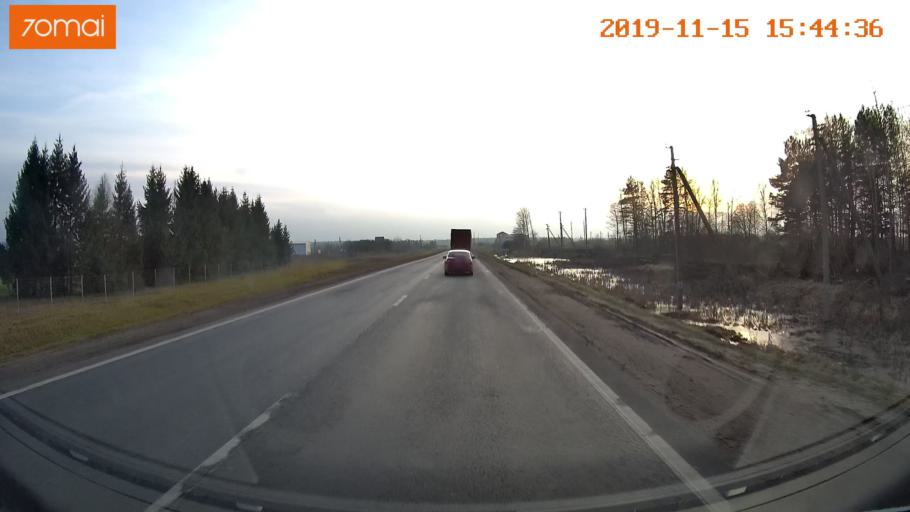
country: RU
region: Jaroslavl
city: Danilov
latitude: 57.9685
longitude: 40.0206
